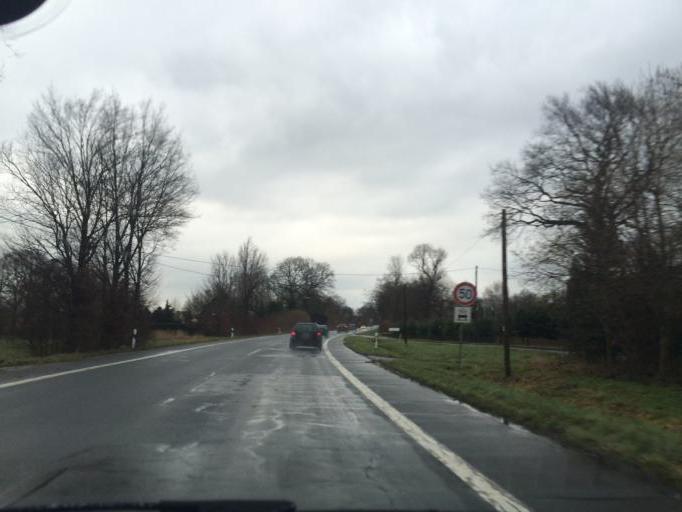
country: DE
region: North Rhine-Westphalia
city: Dorsten
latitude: 51.6419
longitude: 6.9589
